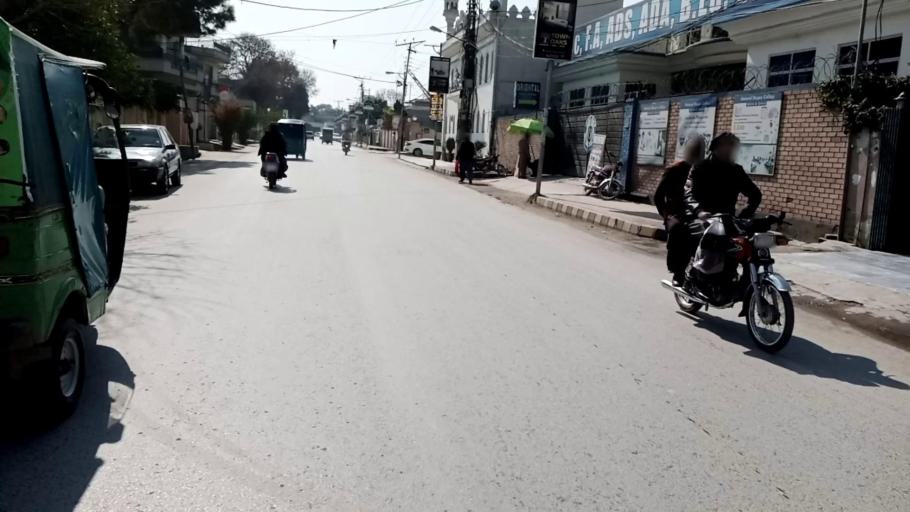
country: PK
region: Khyber Pakhtunkhwa
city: Peshawar
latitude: 33.9997
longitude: 71.5003
